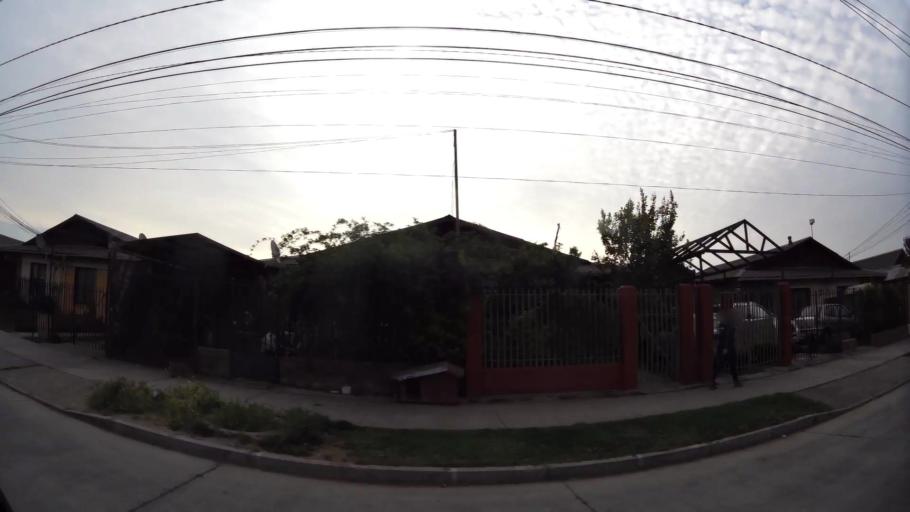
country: CL
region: Santiago Metropolitan
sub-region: Provincia de Talagante
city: Penaflor
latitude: -33.5299
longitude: -70.7979
